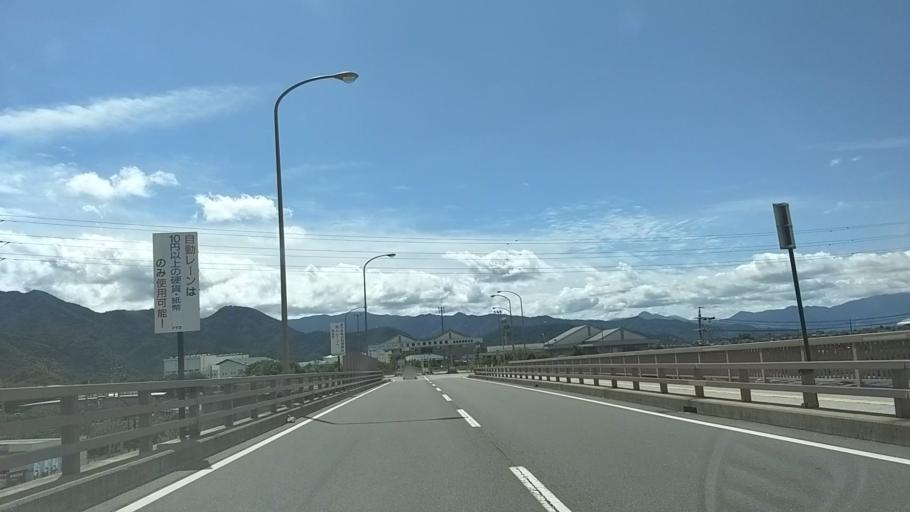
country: JP
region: Nagano
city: Nagano-shi
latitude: 36.6160
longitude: 138.2232
